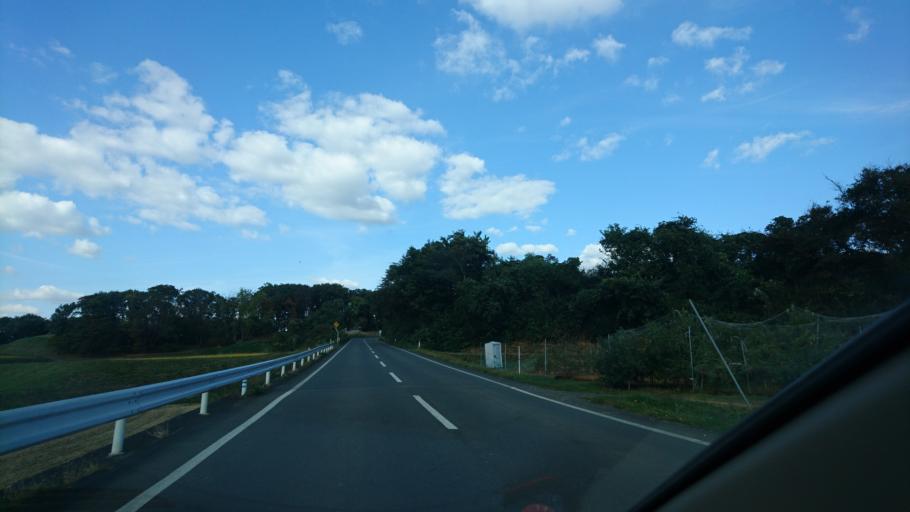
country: JP
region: Iwate
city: Kitakami
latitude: 39.2382
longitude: 141.1334
